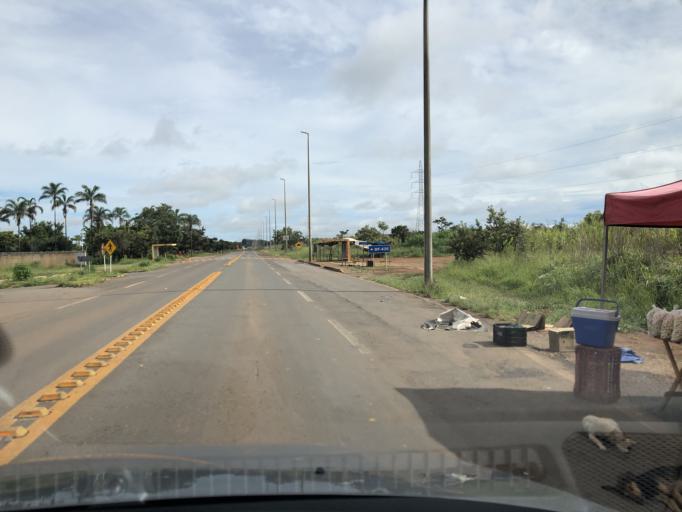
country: BR
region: Federal District
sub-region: Brasilia
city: Brasilia
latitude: -15.6975
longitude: -48.0884
